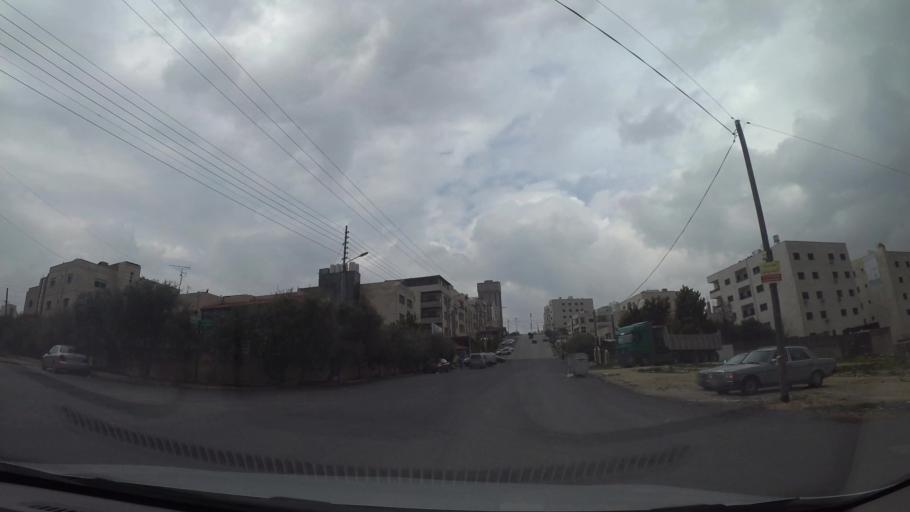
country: JO
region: Amman
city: Umm as Summaq
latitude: 31.8846
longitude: 35.8605
